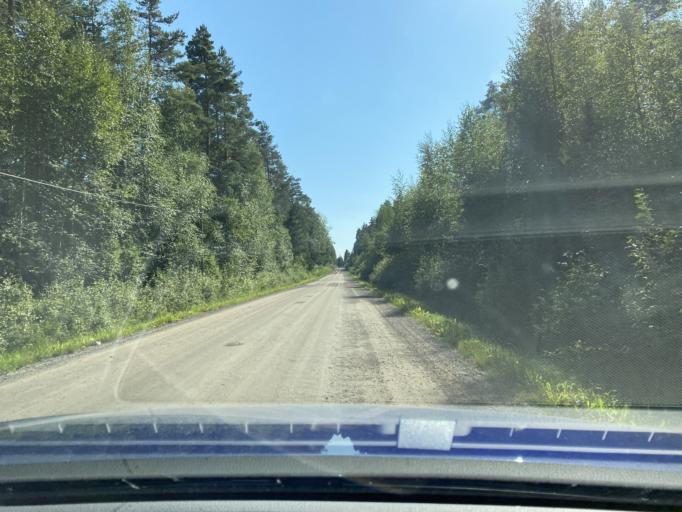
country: FI
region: Satakunta
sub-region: Rauma
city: Kiukainen
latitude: 61.1410
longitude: 21.9948
